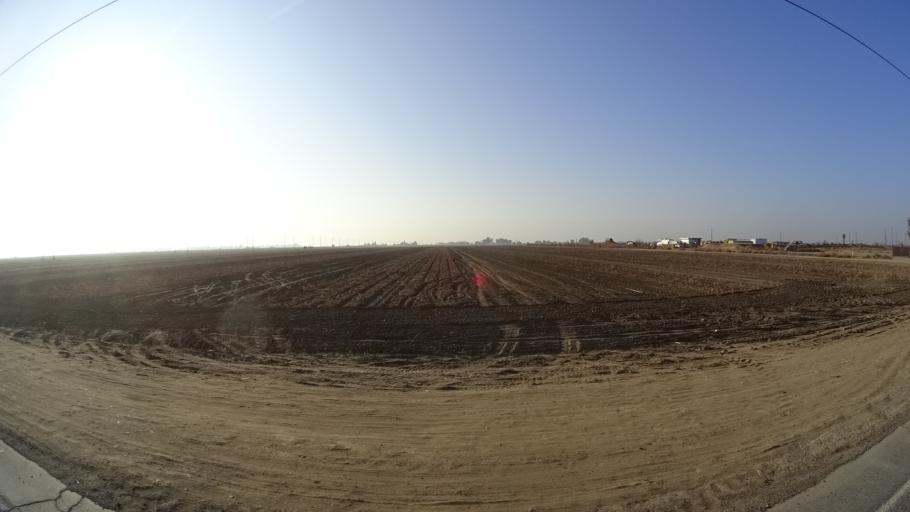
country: US
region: California
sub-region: Kern County
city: Greenfield
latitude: 35.2669
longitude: -118.9785
